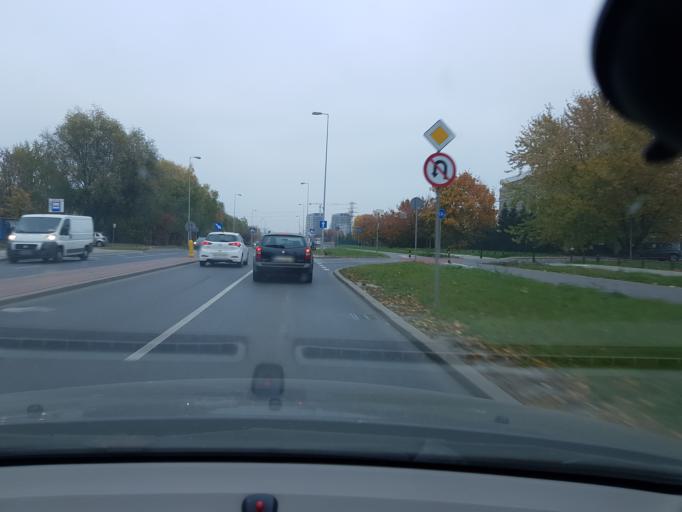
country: PL
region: Masovian Voivodeship
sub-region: Warszawa
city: Ursynow
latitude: 52.1464
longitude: 21.0282
